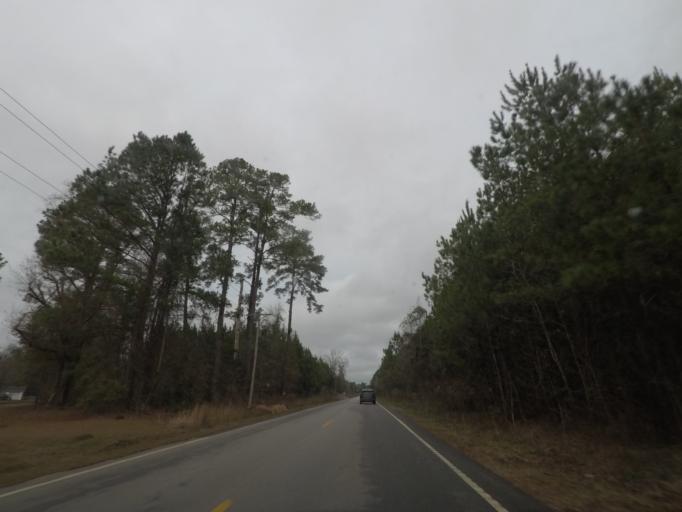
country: US
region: South Carolina
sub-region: Colleton County
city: Walterboro
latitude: 32.8671
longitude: -80.4892
